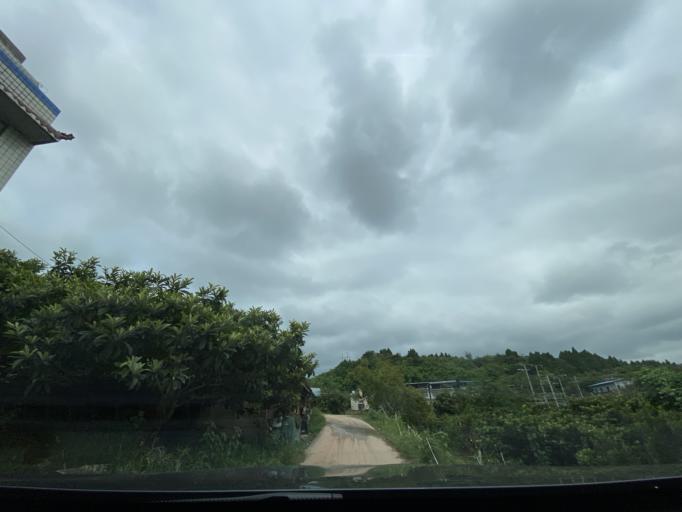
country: CN
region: Sichuan
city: Jiancheng
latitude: 30.4024
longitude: 104.5727
